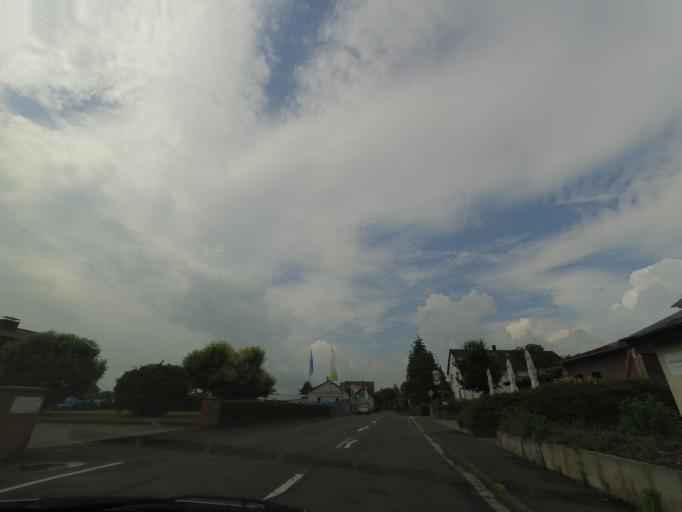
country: DE
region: Hesse
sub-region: Regierungsbezirk Giessen
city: Fronhausen
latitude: 50.7392
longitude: 8.7056
